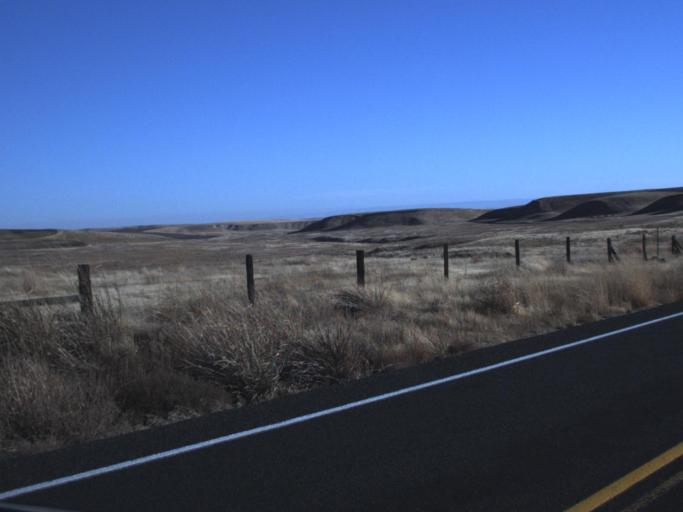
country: US
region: Washington
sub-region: Adams County
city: Ritzville
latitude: 46.8300
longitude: -118.3261
